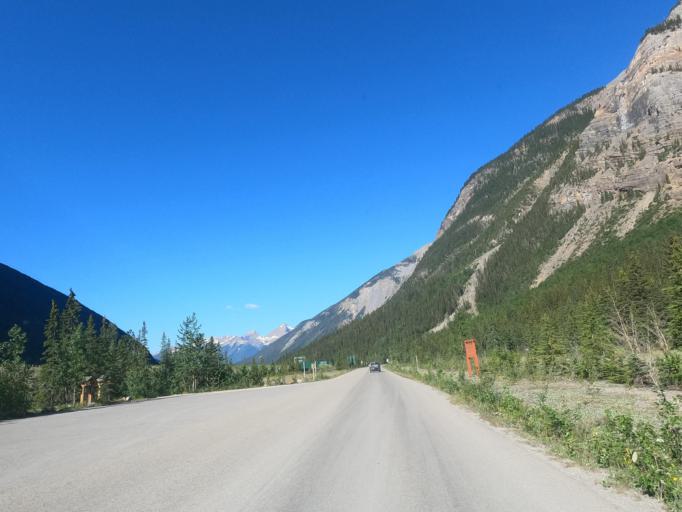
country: CA
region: Alberta
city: Lake Louise
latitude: 51.4206
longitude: -116.4418
